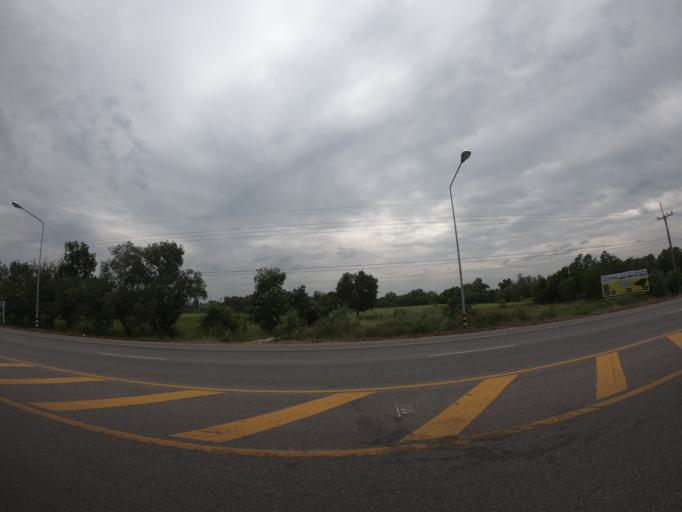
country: TH
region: Roi Et
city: Thawat Buri
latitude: 16.0828
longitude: 103.7300
